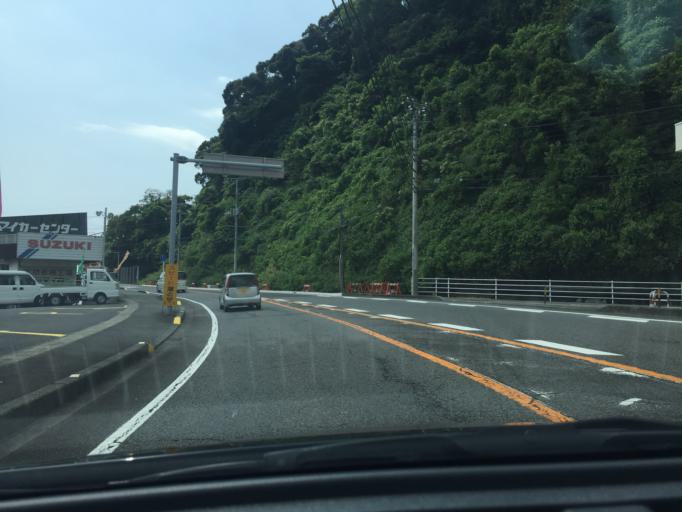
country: JP
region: Shizuoka
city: Ito
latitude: 34.8036
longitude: 139.0585
